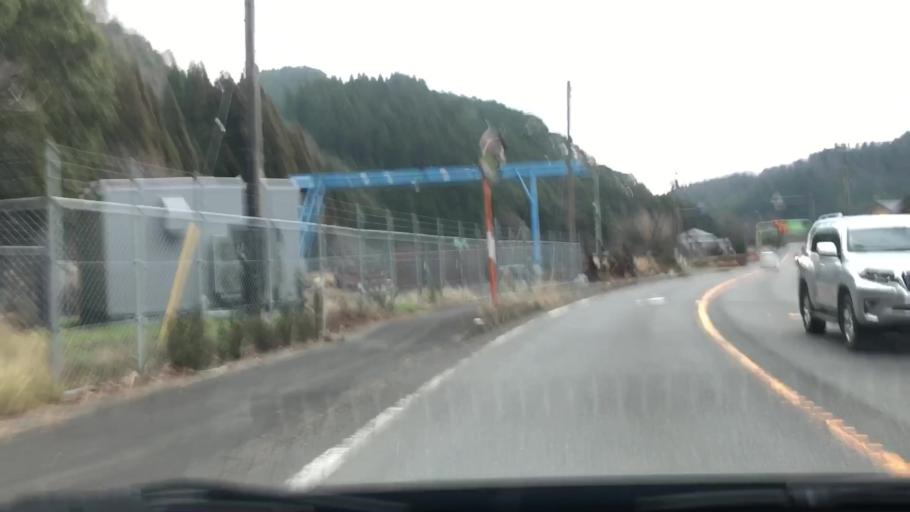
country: JP
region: Oita
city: Saiki
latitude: 32.9889
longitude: 131.8362
